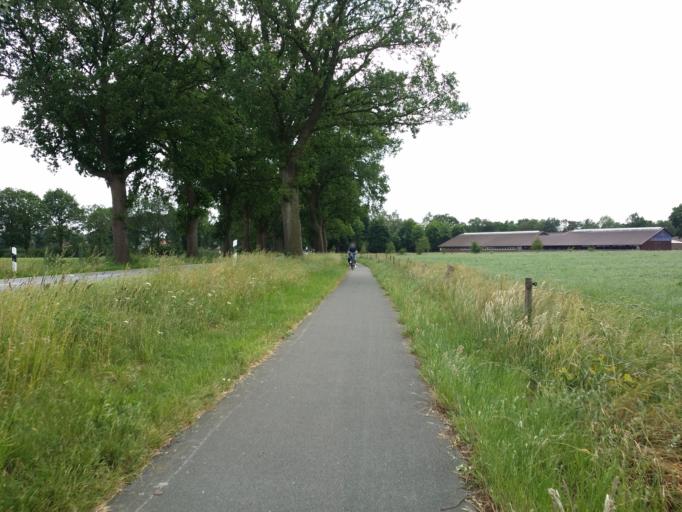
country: DE
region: Lower Saxony
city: Wiefelstede
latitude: 53.2670
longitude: 8.1112
